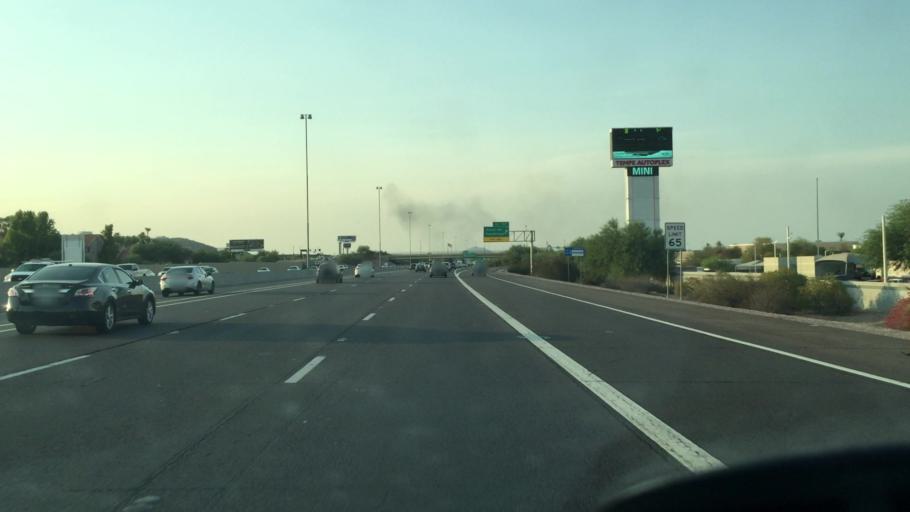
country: US
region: Arizona
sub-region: Maricopa County
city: Guadalupe
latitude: 33.3444
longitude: -111.9748
